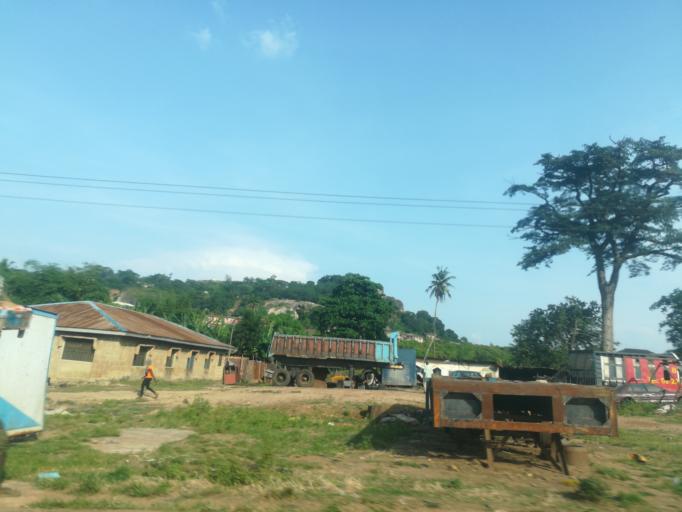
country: NG
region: Oyo
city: Moniya
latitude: 7.4836
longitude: 3.9142
